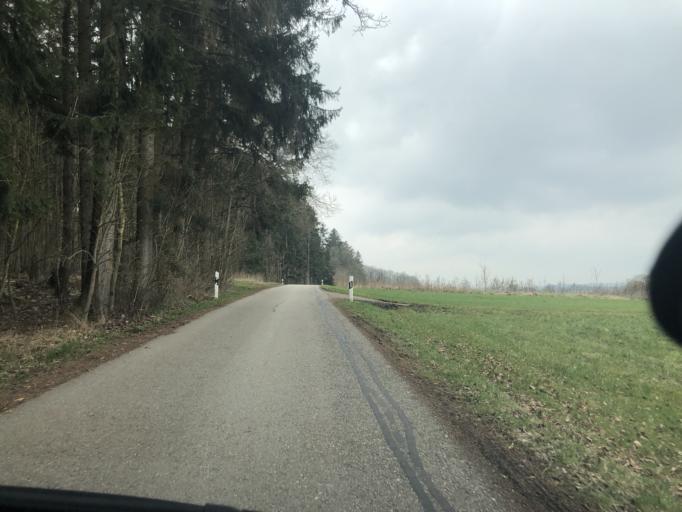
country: DE
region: Bavaria
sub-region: Upper Bavaria
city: Zolling
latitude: 48.4398
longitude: 11.7425
